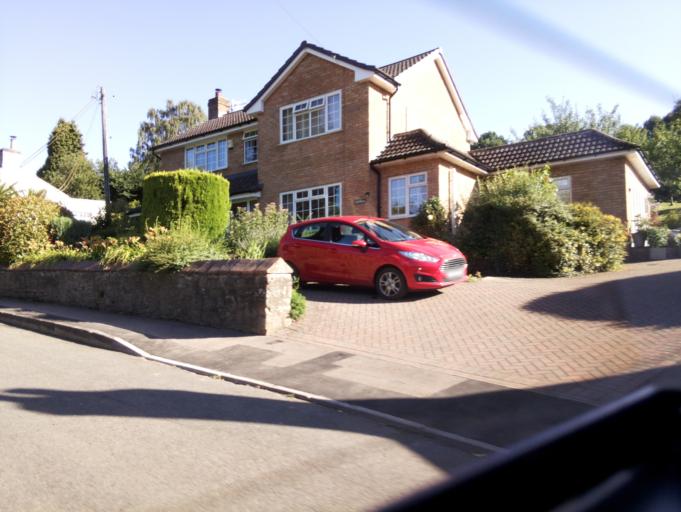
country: GB
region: England
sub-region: Gloucestershire
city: Coleford
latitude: 51.7808
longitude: -2.6452
